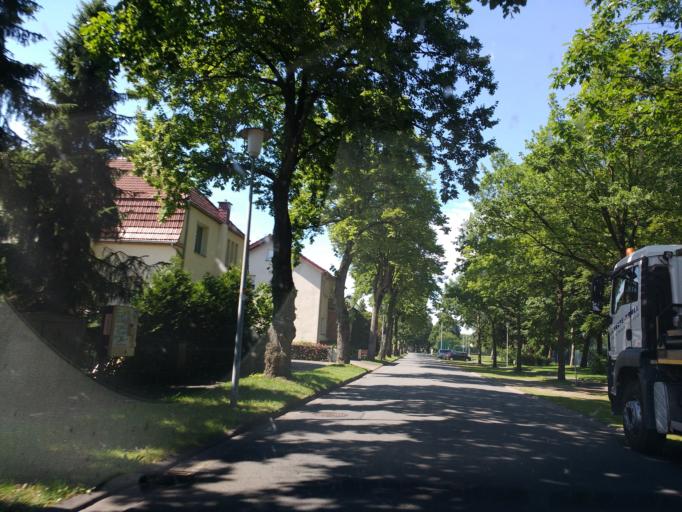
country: DE
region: North Rhine-Westphalia
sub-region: Regierungsbezirk Detmold
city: Schlangen
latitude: 51.8104
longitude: 8.8382
